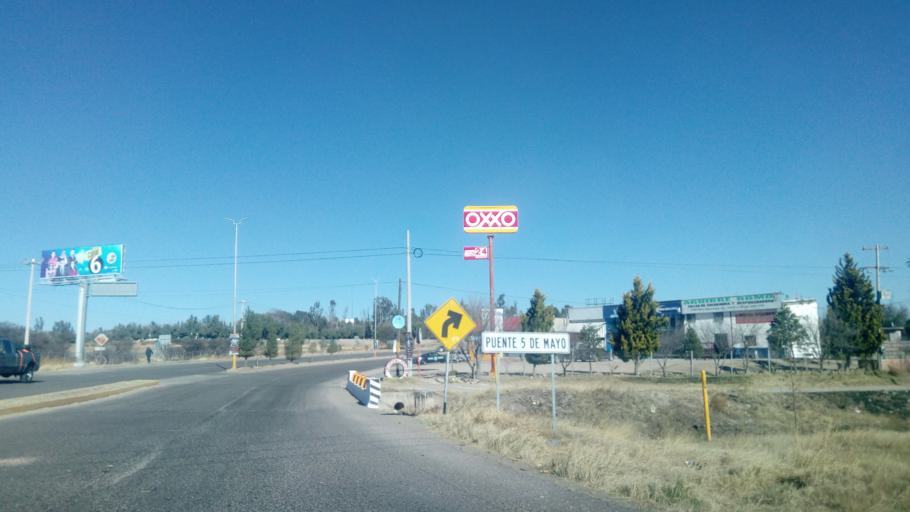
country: MX
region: Durango
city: Victoria de Durango
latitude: 24.0961
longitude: -104.5762
